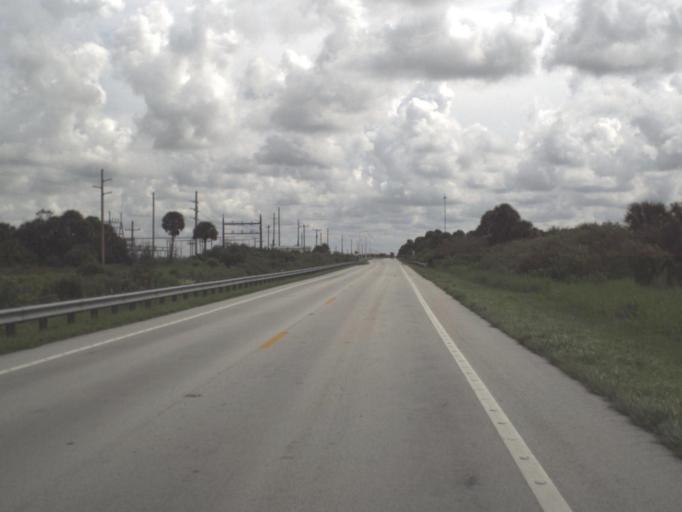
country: US
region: Florida
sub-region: Glades County
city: Buckhead Ridge
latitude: 27.2361
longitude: -81.0731
